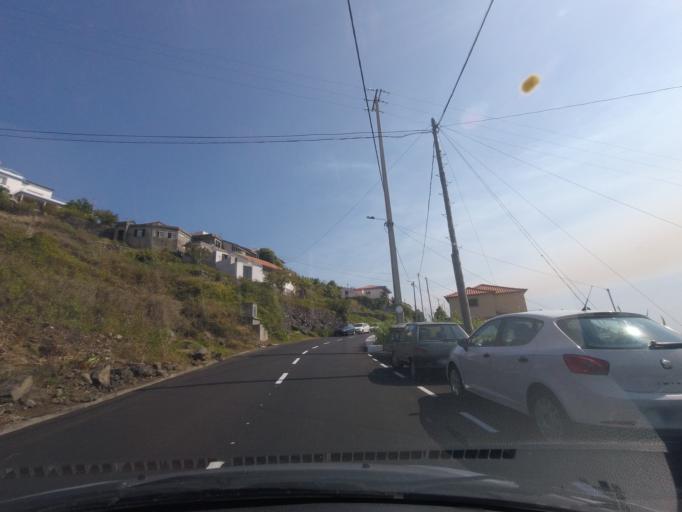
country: PT
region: Madeira
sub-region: Ribeira Brava
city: Campanario
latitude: 32.6692
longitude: -17.0526
